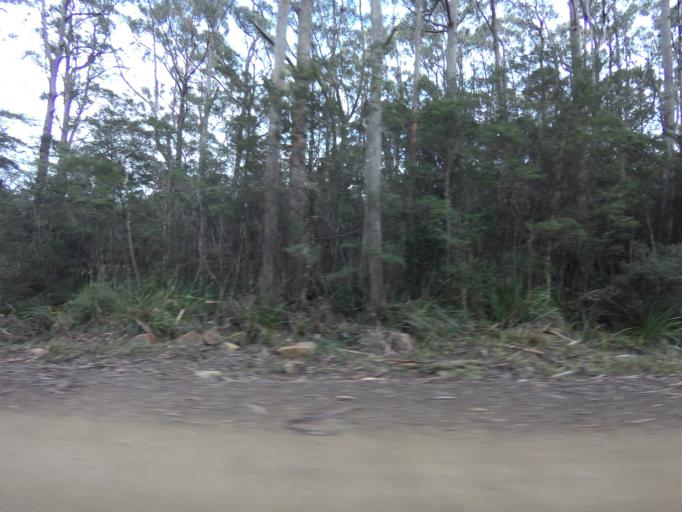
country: AU
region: Tasmania
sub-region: Huon Valley
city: Geeveston
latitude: -43.5415
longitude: 146.8924
